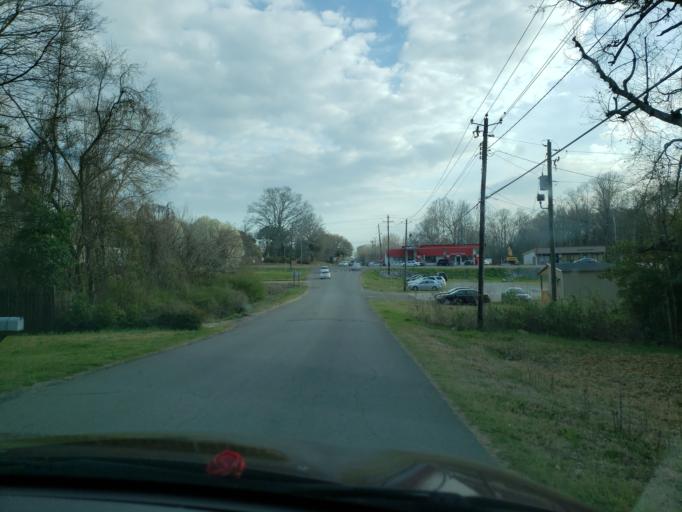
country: US
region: Alabama
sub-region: Hale County
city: Greensboro
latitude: 32.6997
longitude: -87.5922
